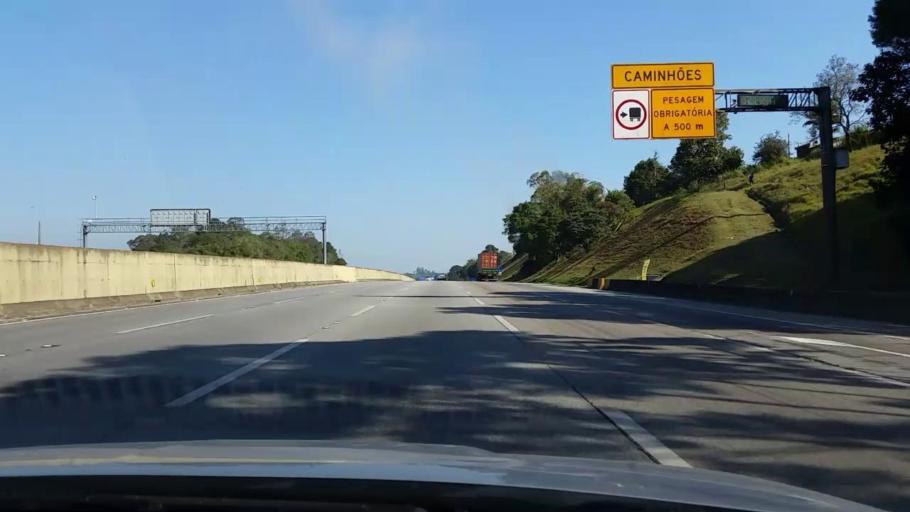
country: BR
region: Sao Paulo
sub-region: Sao Bernardo Do Campo
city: Sao Bernardo do Campo
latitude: -23.7763
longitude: -46.5956
